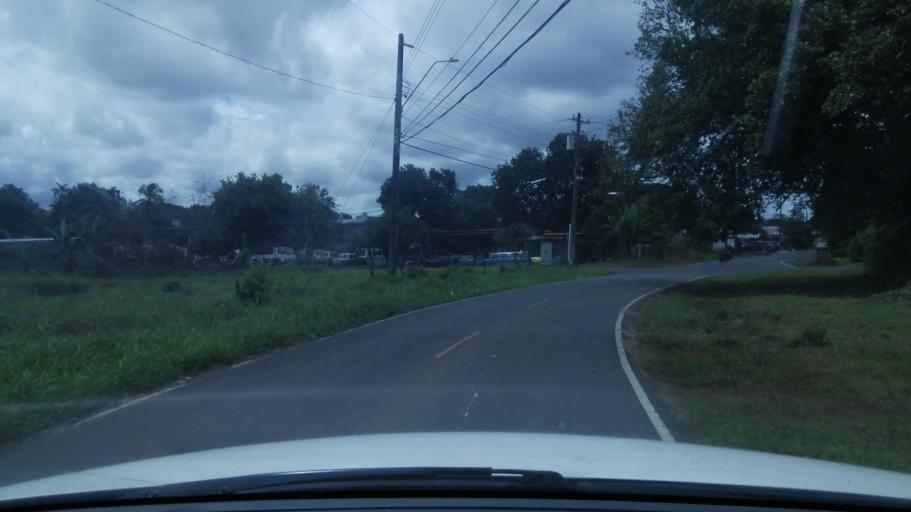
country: PA
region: Chiriqui
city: David
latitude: 8.4172
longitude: -82.4291
